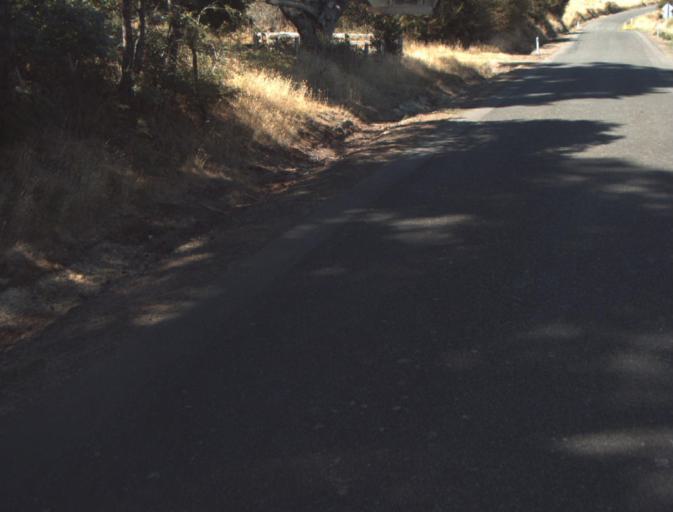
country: AU
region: Tasmania
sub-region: Launceston
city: Newstead
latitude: -41.3508
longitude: 147.3035
